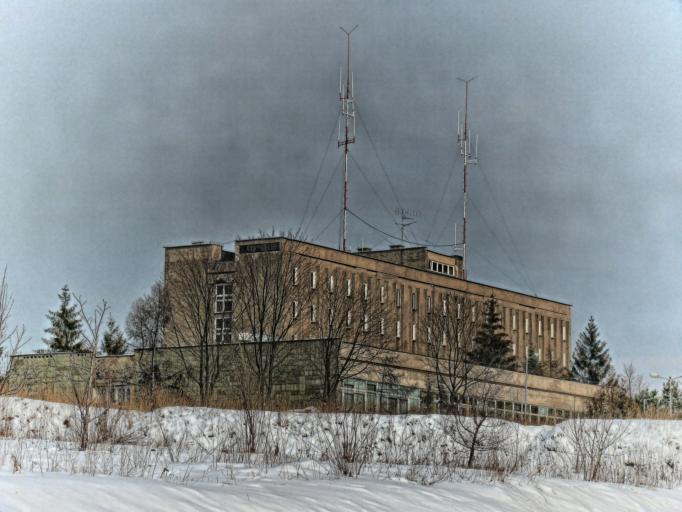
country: PL
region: Lublin Voivodeship
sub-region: Powiat lubelski
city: Lublin
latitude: 51.2550
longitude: 22.5589
